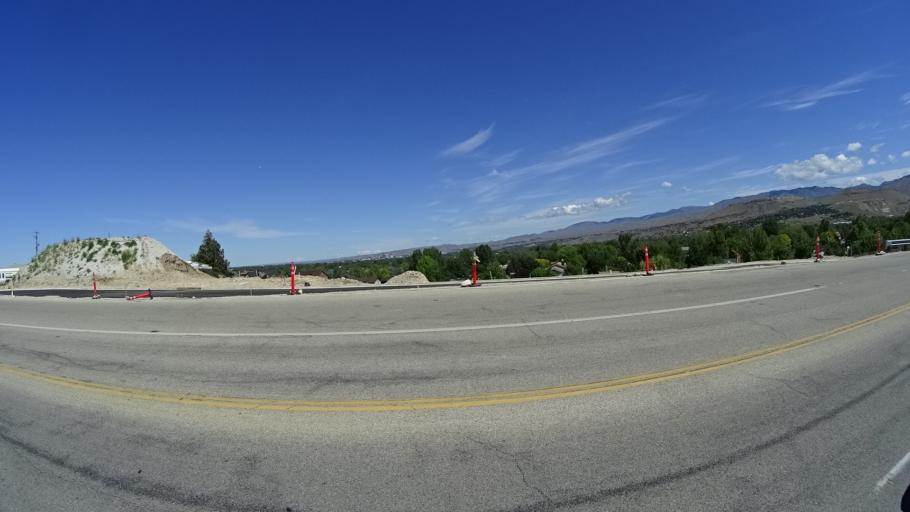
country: US
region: Idaho
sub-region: Ada County
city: Boise
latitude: 43.5609
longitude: -116.1677
